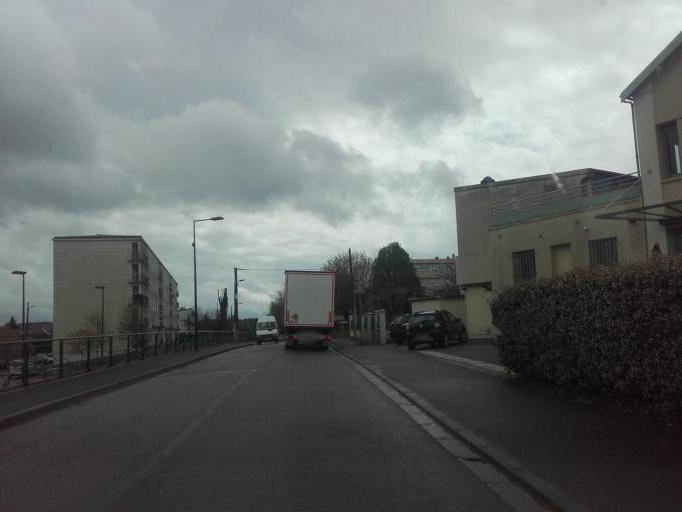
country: FR
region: Bourgogne
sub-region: Departement de l'Yonne
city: Chablis
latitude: 47.8124
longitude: 3.7965
